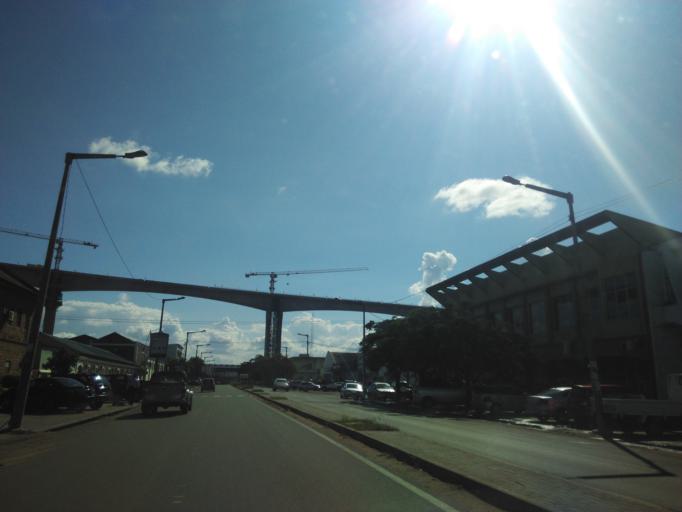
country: MZ
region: Maputo City
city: Maputo
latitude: -25.9677
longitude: 32.5626
